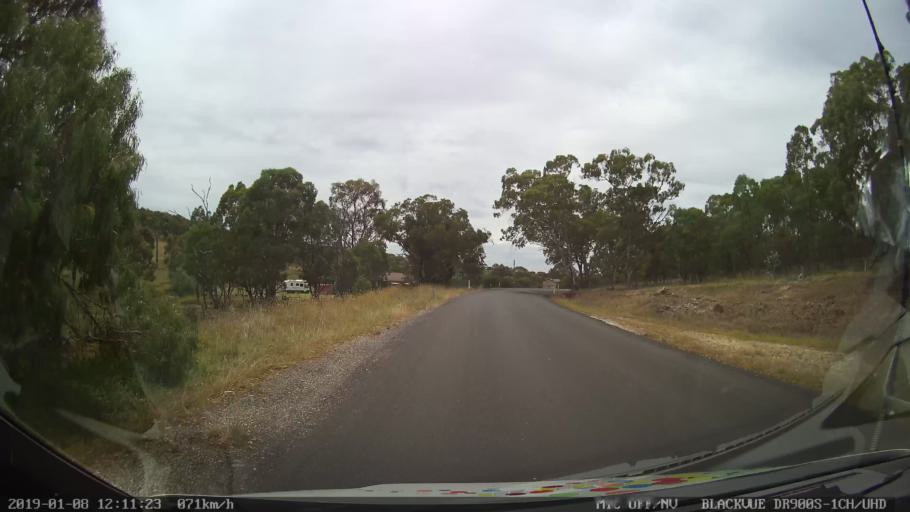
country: AU
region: New South Wales
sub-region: Armidale Dumaresq
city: Armidale
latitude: -30.4505
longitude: 151.5952
